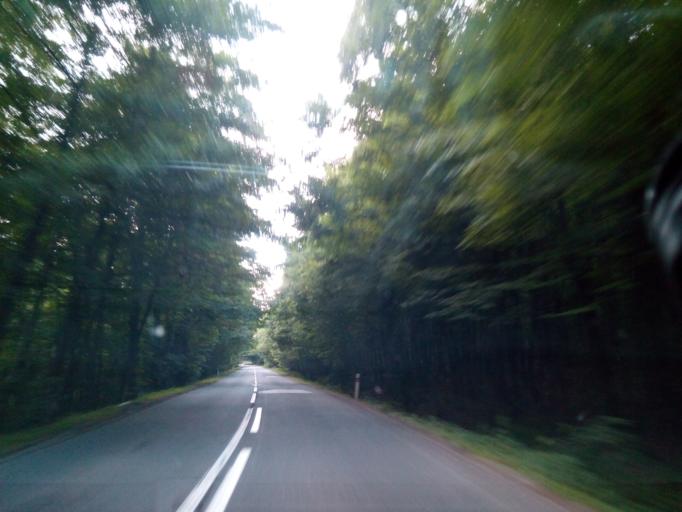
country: SK
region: Kosicky
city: Kosice
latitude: 48.6396
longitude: 21.4419
